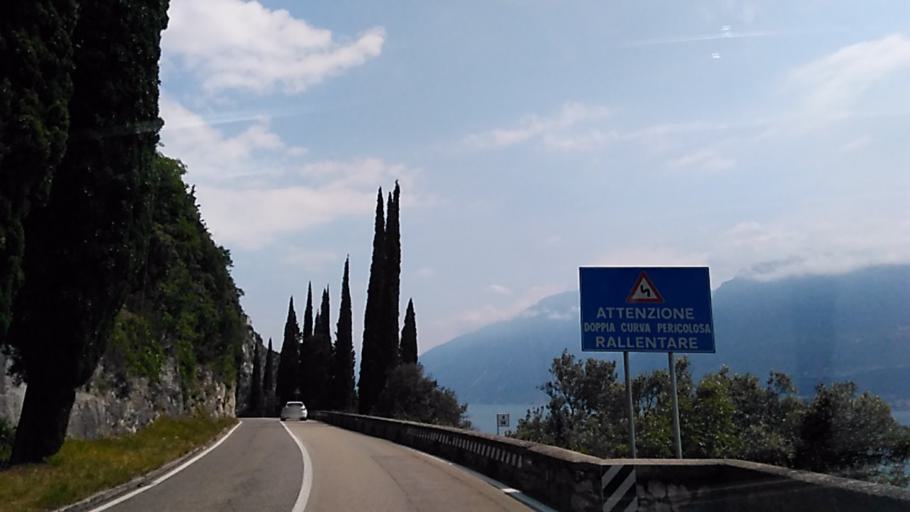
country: IT
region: Lombardy
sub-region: Provincia di Brescia
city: Pieve
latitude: 45.7643
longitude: 10.7581
